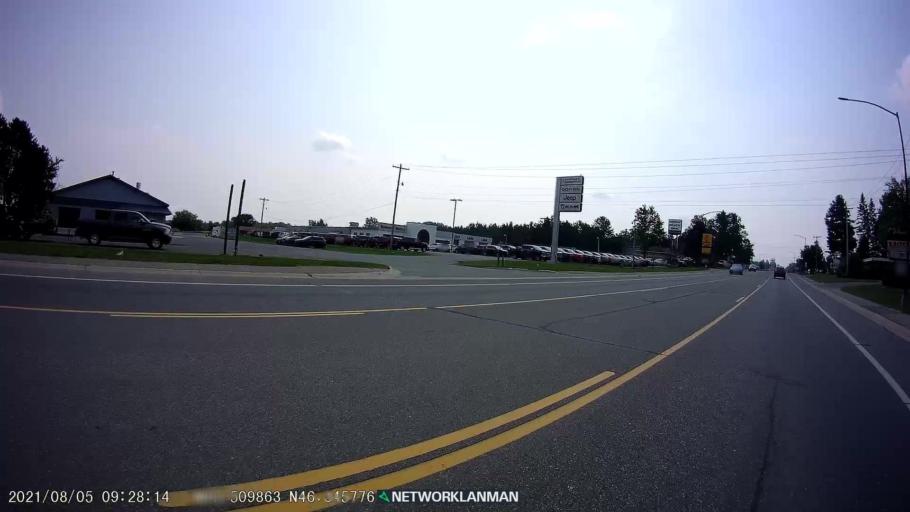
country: US
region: Michigan
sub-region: Luce County
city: Newberry
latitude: 46.3455
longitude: -85.5099
